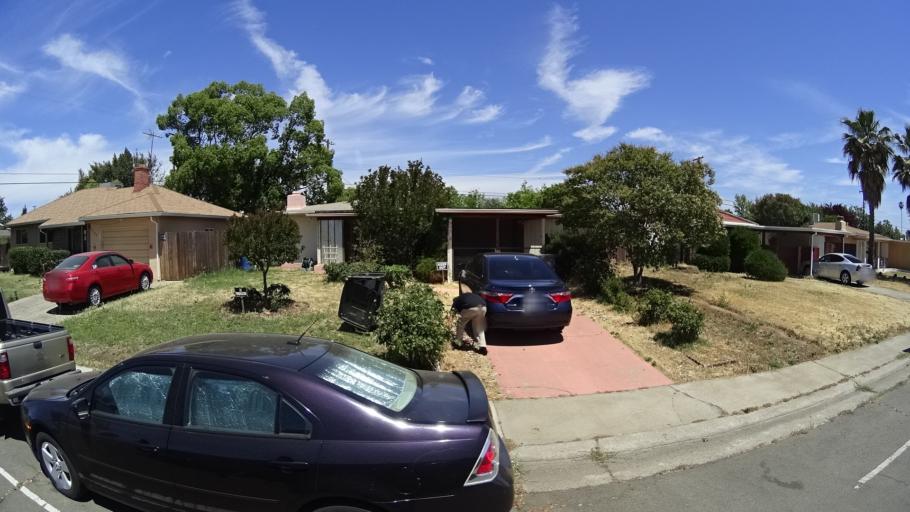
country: US
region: California
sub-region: Sacramento County
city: Parkway
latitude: 38.5222
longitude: -121.4359
